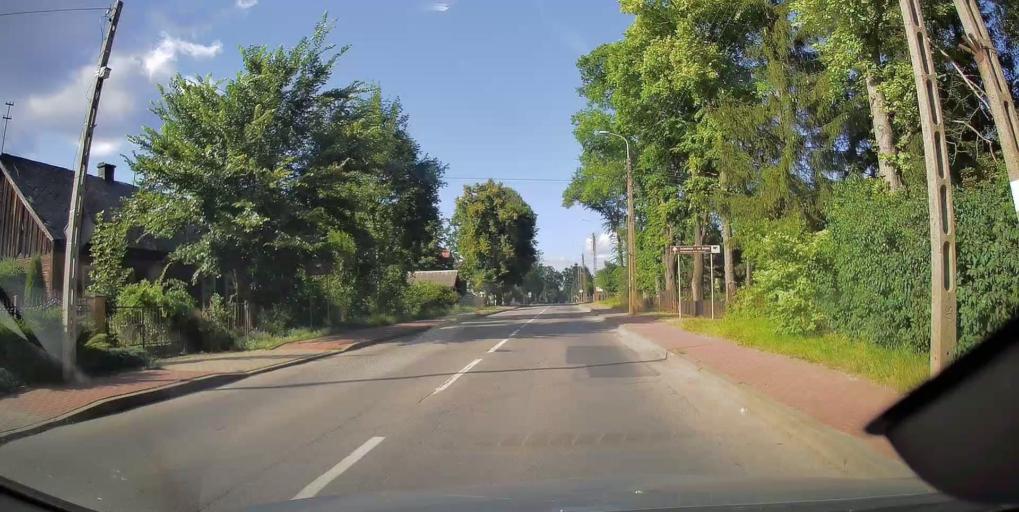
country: PL
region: Swietokrzyskie
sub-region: Powiat skarzyski
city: Suchedniow
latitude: 51.0400
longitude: 20.8354
